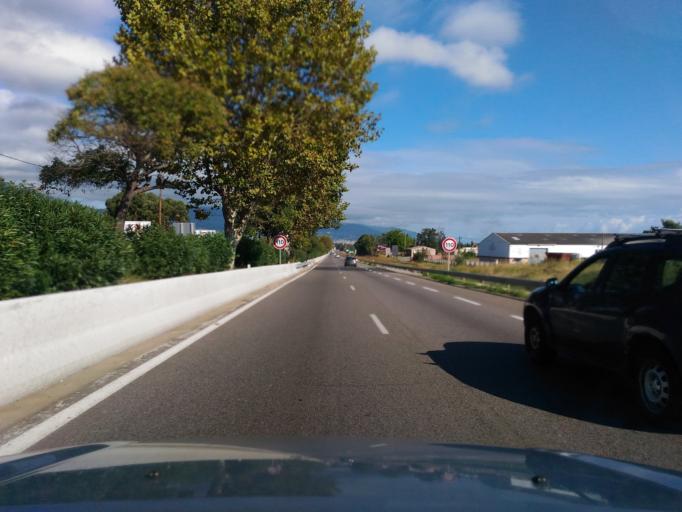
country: FR
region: Corsica
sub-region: Departement de la Haute-Corse
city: Biguglia
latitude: 42.5963
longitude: 9.4388
